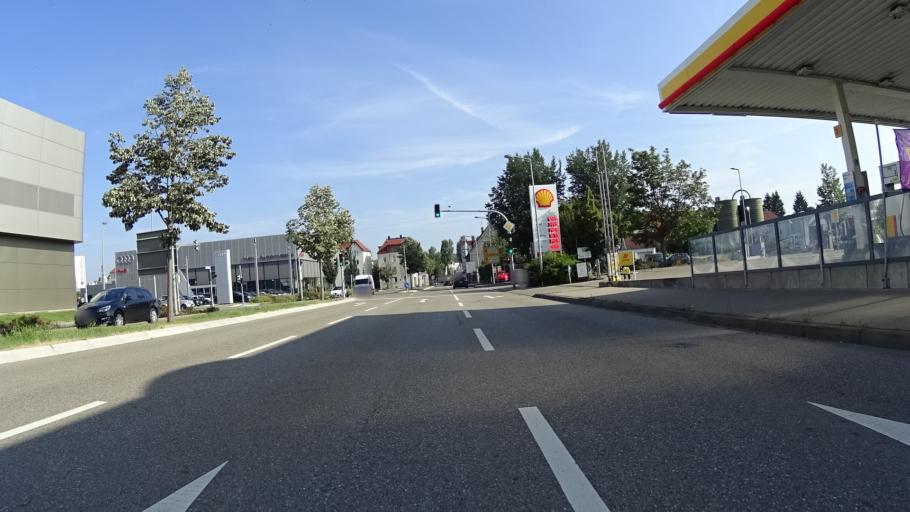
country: DE
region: Baden-Wuerttemberg
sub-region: Regierungsbezirk Stuttgart
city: Goeppingen
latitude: 48.6955
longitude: 9.6648
